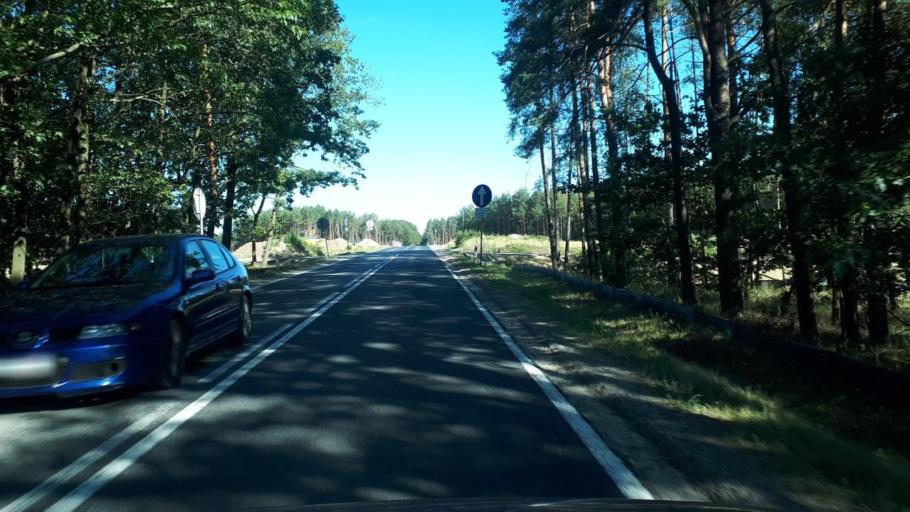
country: PL
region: Silesian Voivodeship
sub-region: Powiat lubliniecki
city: Sierakow Slaski
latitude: 50.8172
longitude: 18.5403
